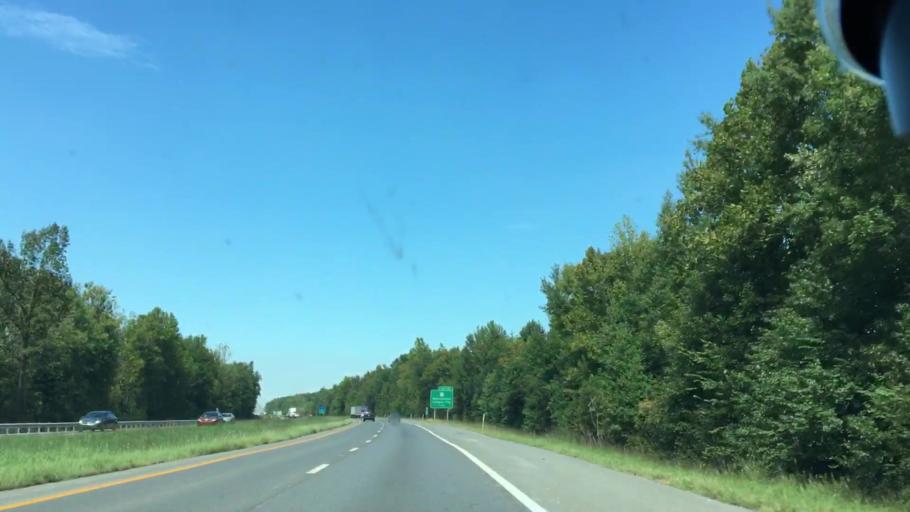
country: US
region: Kentucky
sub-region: Hopkins County
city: Madisonville
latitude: 37.3089
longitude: -87.4674
